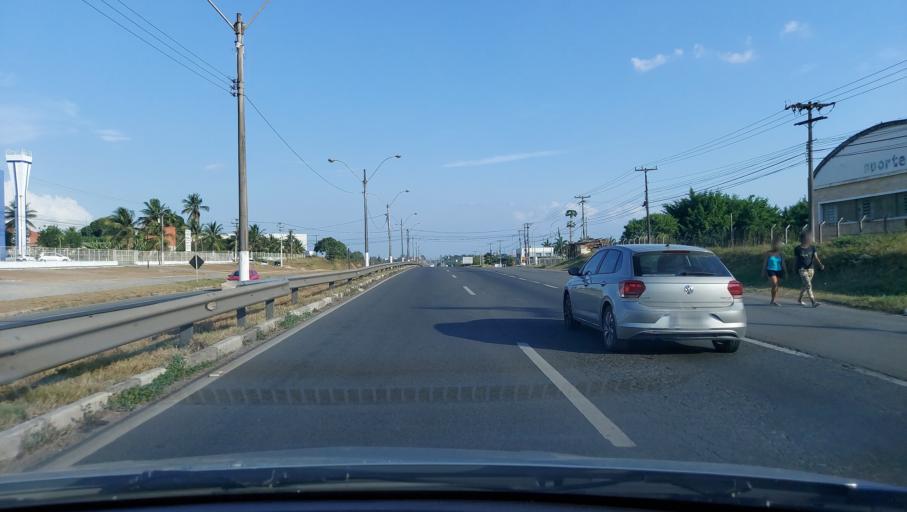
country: BR
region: Bahia
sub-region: Feira De Santana
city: Feira de Santana
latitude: -12.2814
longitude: -38.9235
